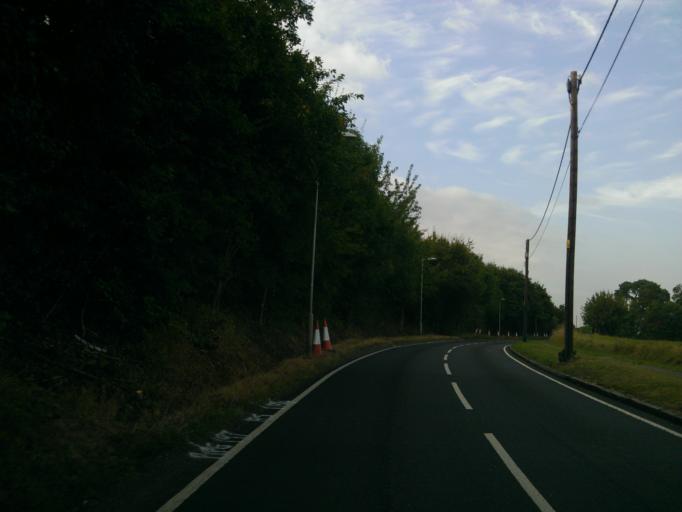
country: GB
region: England
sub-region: Essex
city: Witham
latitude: 51.8200
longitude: 0.6586
